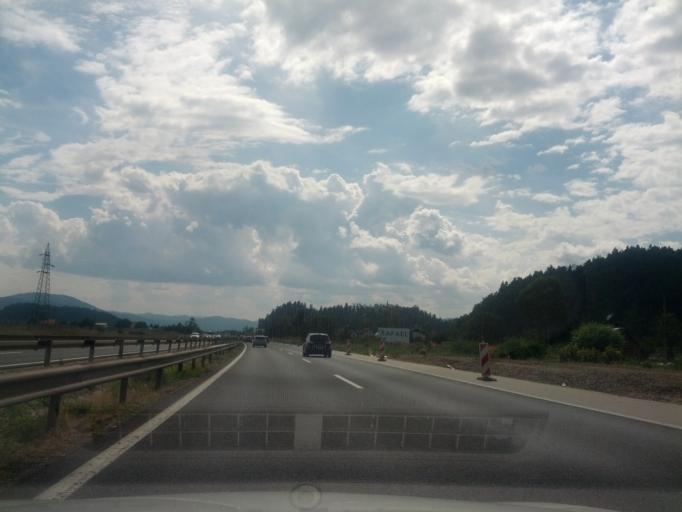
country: SI
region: Log-Dragomer
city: Dragomer
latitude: 46.0152
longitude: 14.3829
